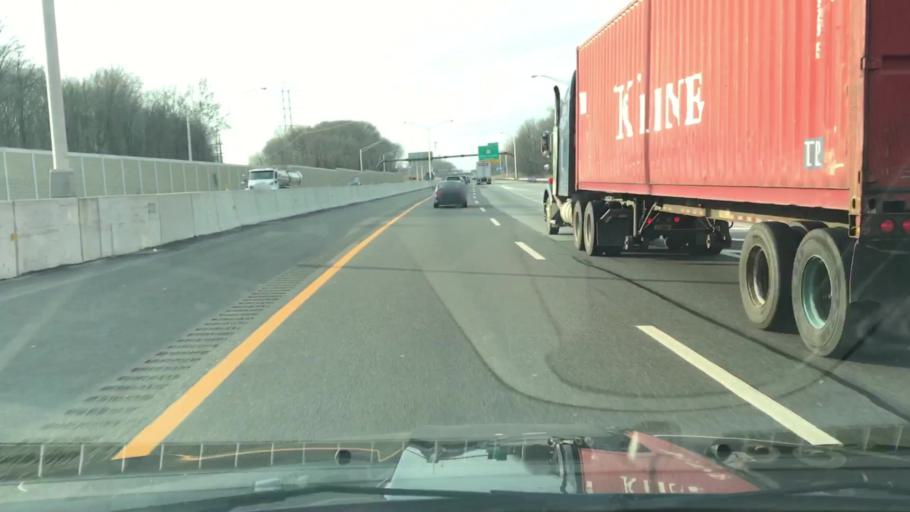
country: US
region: Pennsylvania
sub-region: Bucks County
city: Trevose
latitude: 40.1283
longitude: -74.9538
